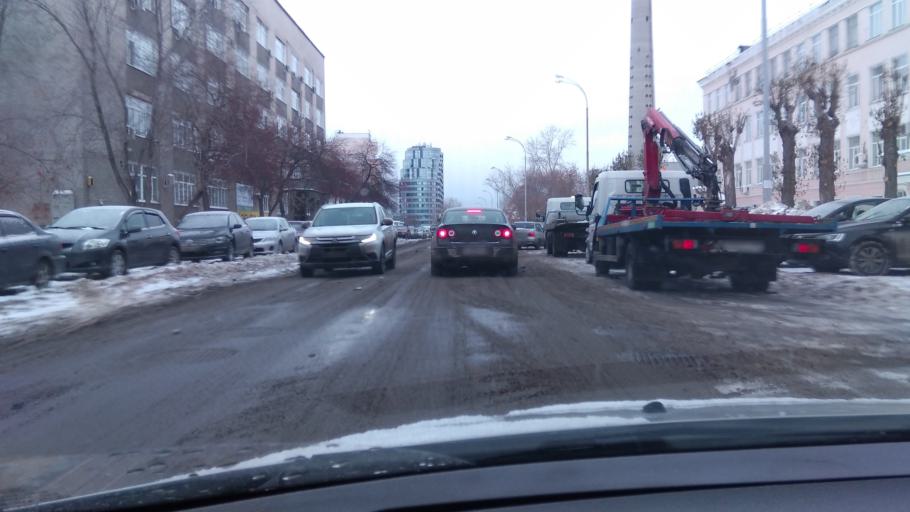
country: RU
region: Sverdlovsk
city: Yekaterinburg
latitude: 56.8204
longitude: 60.6088
